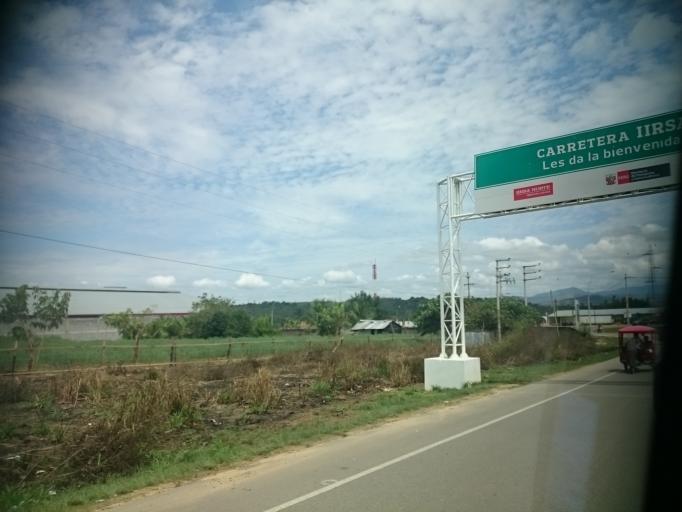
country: PE
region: San Martin
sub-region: Provincia de San Martin
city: Tarapoto
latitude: -6.5074
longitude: -76.3465
